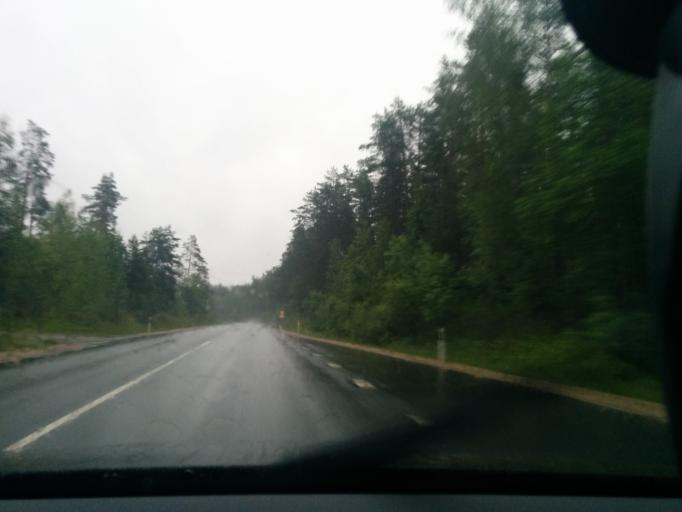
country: LV
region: Ikskile
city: Ikskile
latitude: 56.8935
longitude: 24.4469
